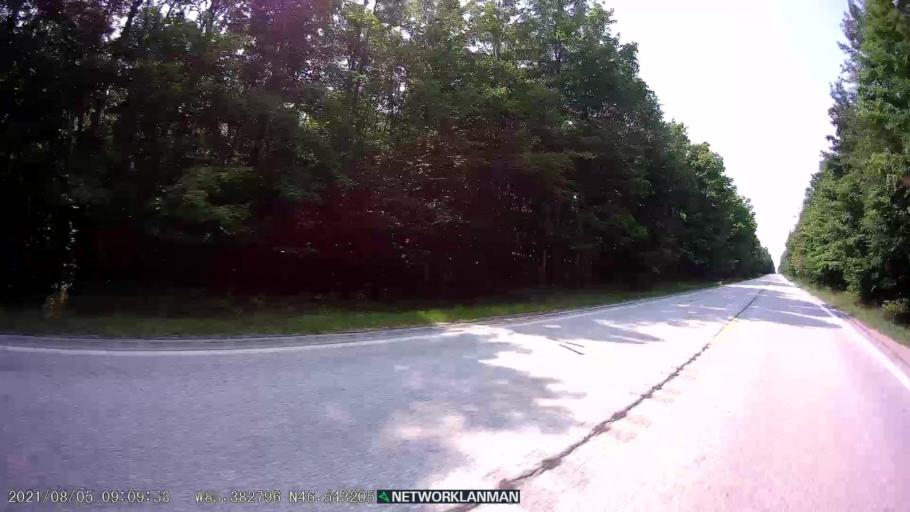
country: US
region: Michigan
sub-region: Luce County
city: Newberry
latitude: 46.5430
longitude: -85.3832
